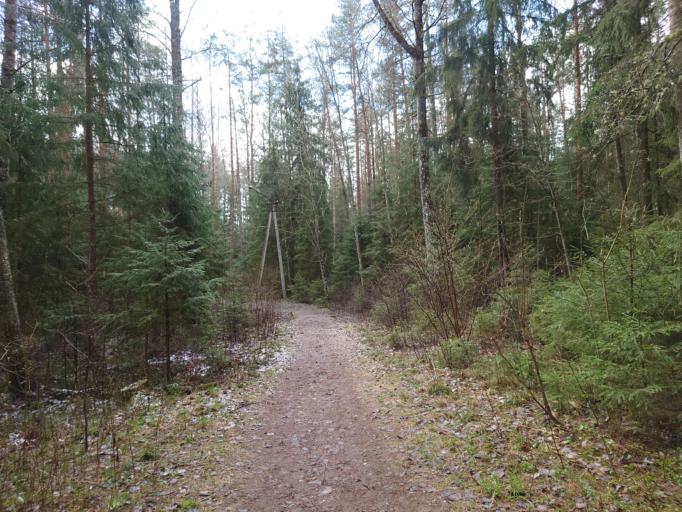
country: EE
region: Vorumaa
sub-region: Voru linn
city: Voru
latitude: 57.9093
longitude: 26.9796
